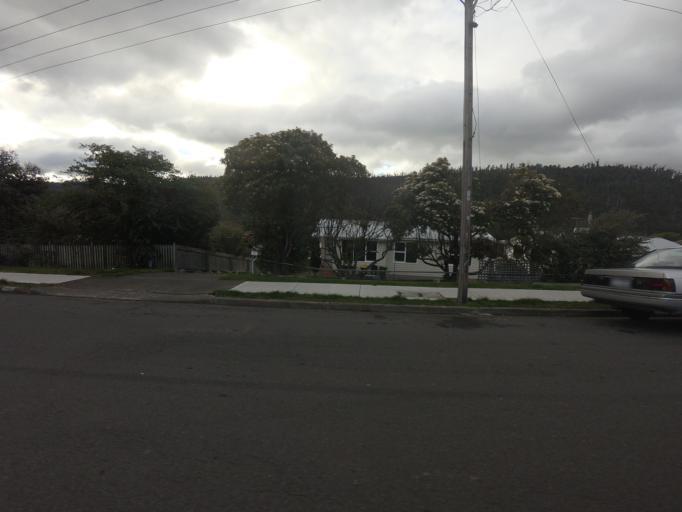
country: AU
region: Tasmania
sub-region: Clarence
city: Warrane
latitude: -42.8583
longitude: 147.4043
